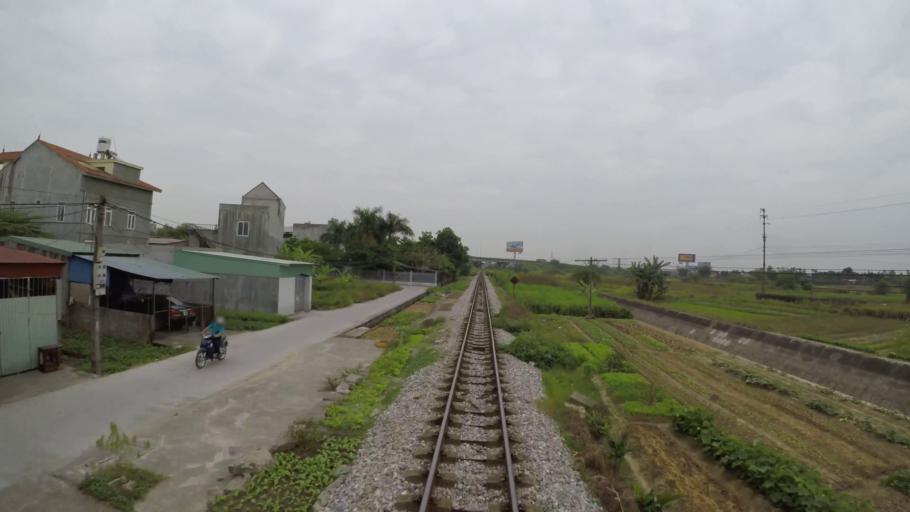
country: VN
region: Hai Phong
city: An Duong
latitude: 20.9127
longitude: 106.5678
